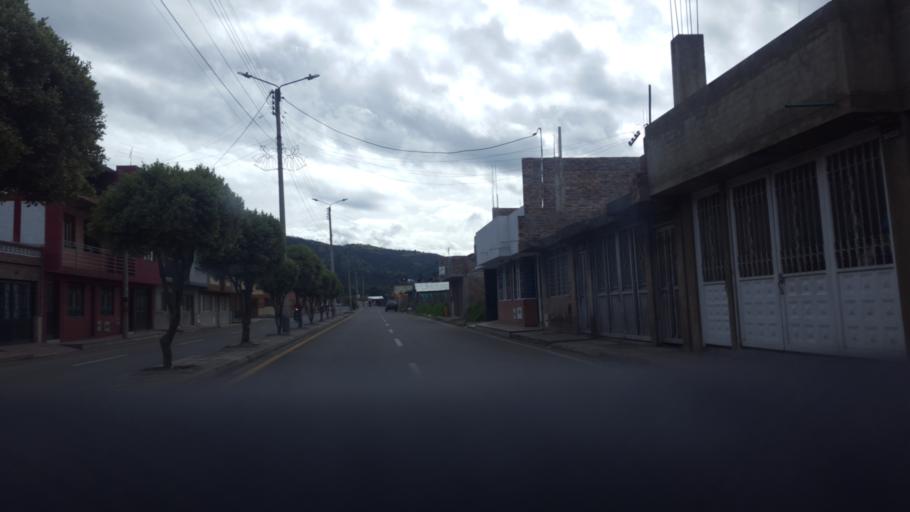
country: CO
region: Boyaca
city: Belen
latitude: 5.9900
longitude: -72.9101
